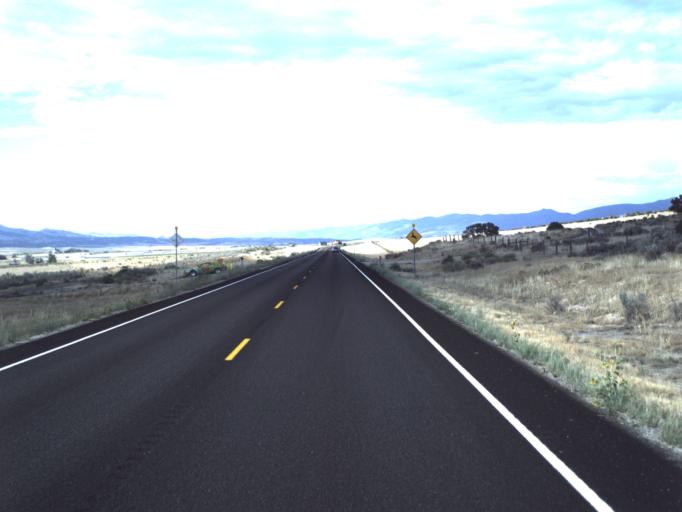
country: US
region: Utah
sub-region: Sanpete County
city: Moroni
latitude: 39.4500
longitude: -111.5440
